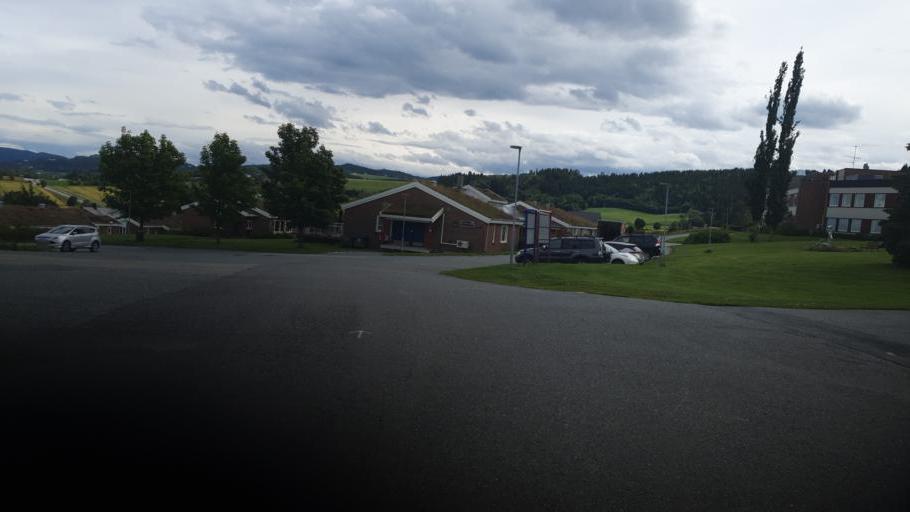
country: NO
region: Sor-Trondelag
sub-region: Malvik
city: Malvik
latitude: 63.4369
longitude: 10.6556
